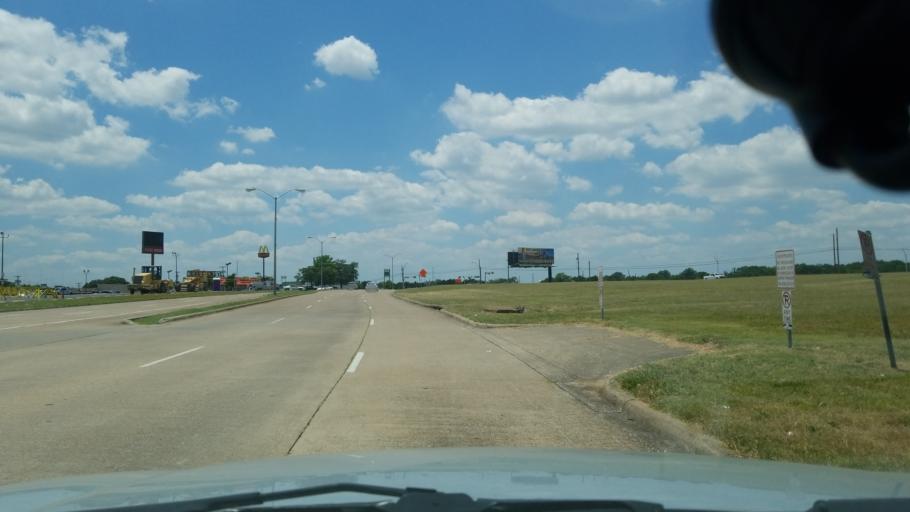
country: US
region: Texas
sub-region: Dallas County
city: Duncanville
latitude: 32.6716
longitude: -96.8586
